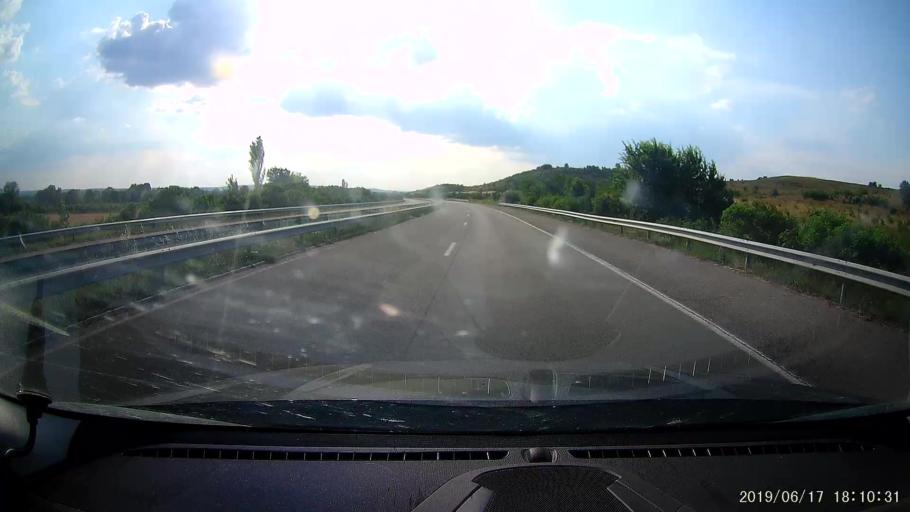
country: BG
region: Khaskovo
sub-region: Obshtina Lyubimets
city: Lyubimets
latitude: 41.8753
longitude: 26.0756
